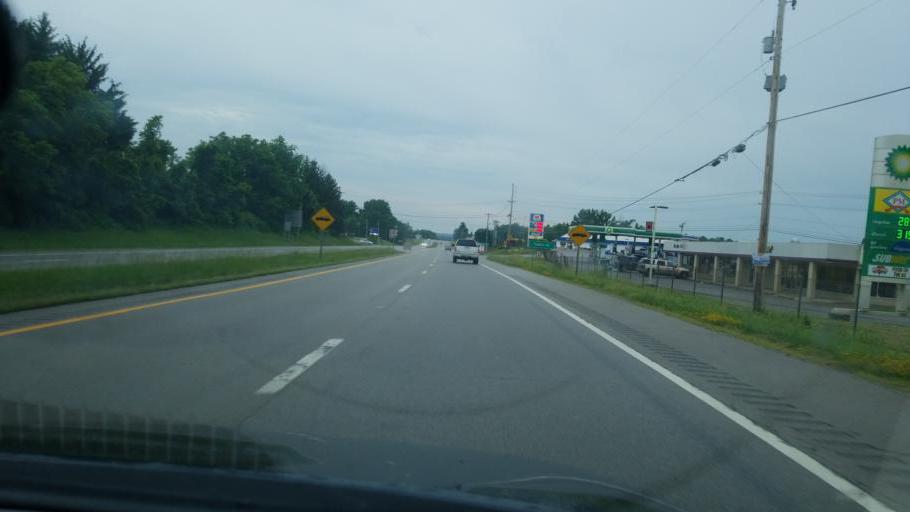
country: US
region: West Virginia
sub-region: Wood County
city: Washington
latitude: 39.2784
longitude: -81.6867
